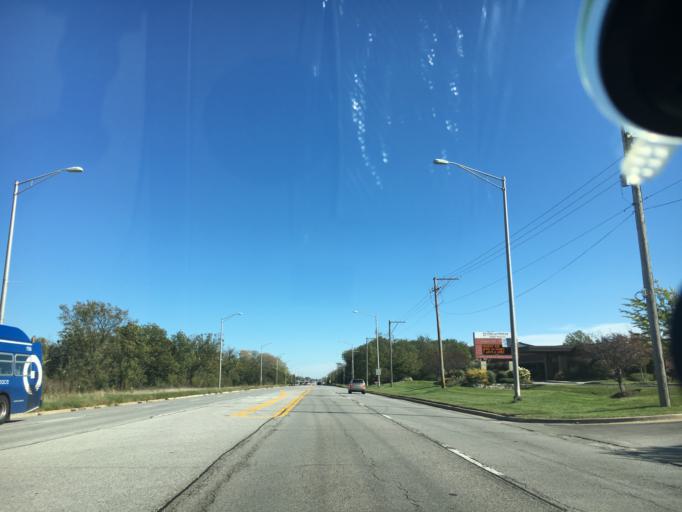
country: US
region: Illinois
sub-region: Cook County
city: Tinley Park
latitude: 41.6024
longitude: -87.7824
